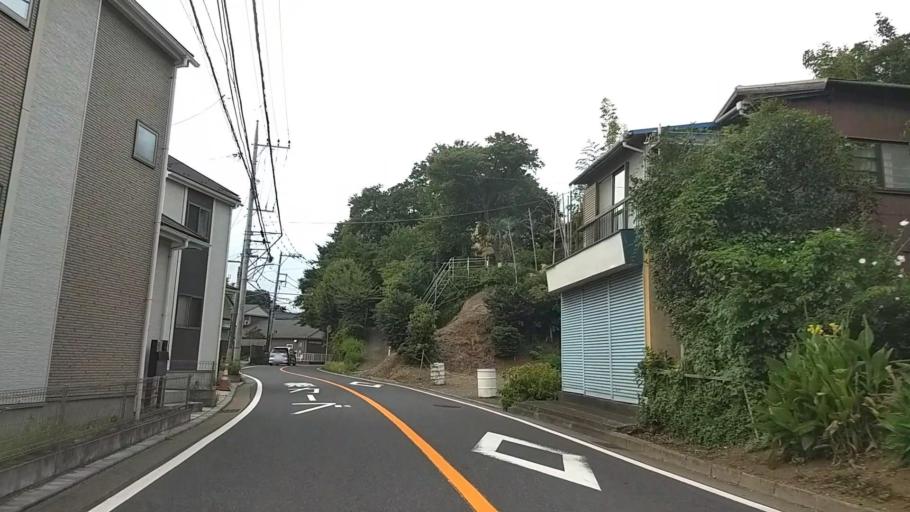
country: JP
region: Kanagawa
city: Yokohama
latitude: 35.4896
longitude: 139.5716
